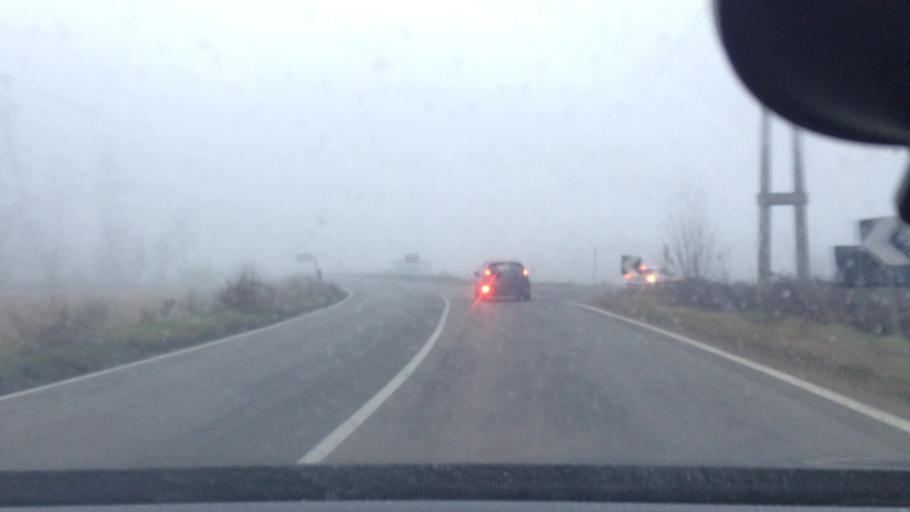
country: IT
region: Lombardy
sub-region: Citta metropolitana di Milano
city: Cantalupo
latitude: 45.5714
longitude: 8.9982
